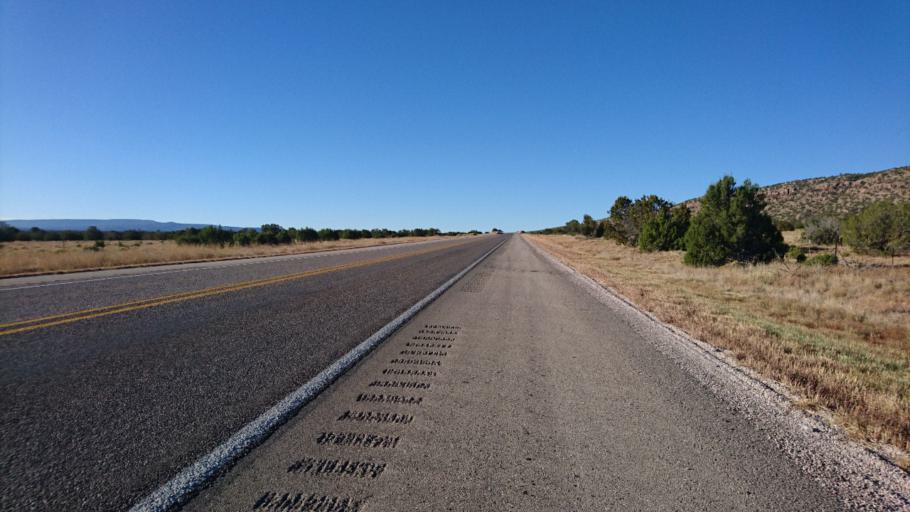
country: US
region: New Mexico
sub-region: Cibola County
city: Grants
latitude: 35.0005
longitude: -107.8953
